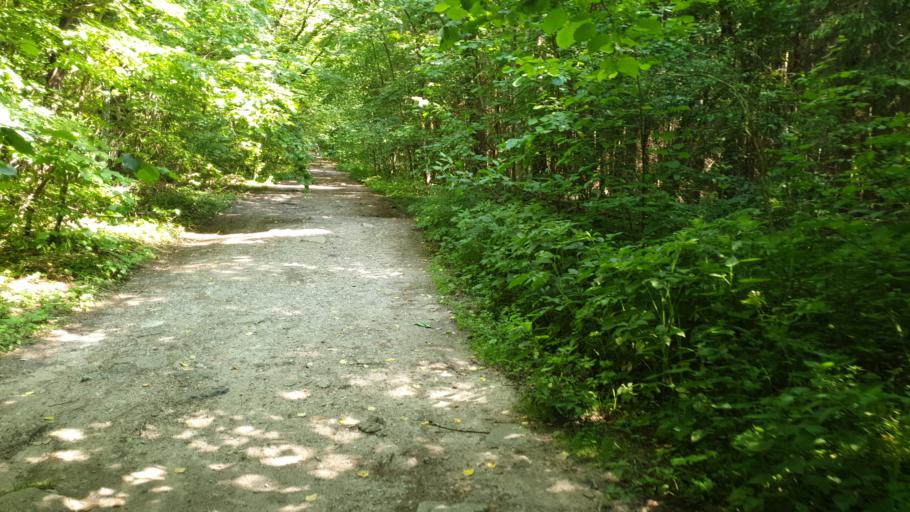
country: LT
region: Vilnius County
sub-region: Vilnius
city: Fabijoniskes
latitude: 54.7893
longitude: 25.3131
